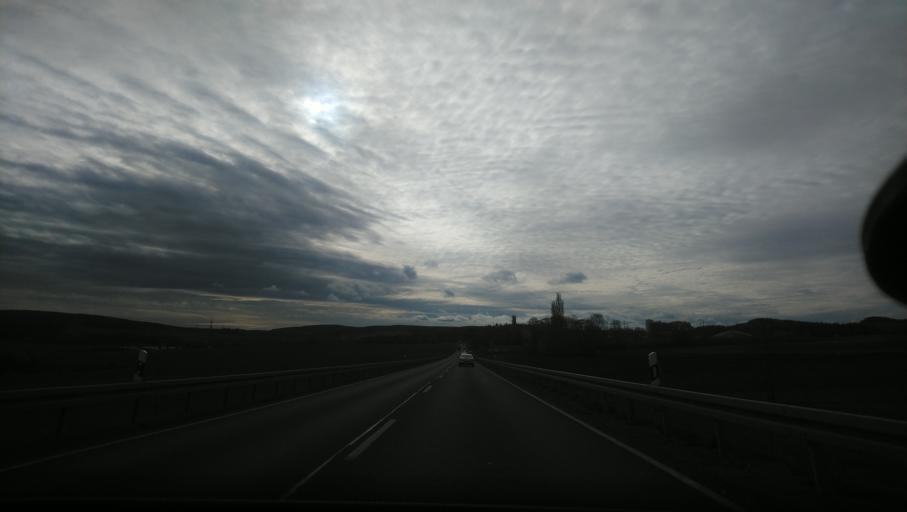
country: DE
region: Saxony
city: Dorfchemnitz
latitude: 50.6628
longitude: 12.8090
